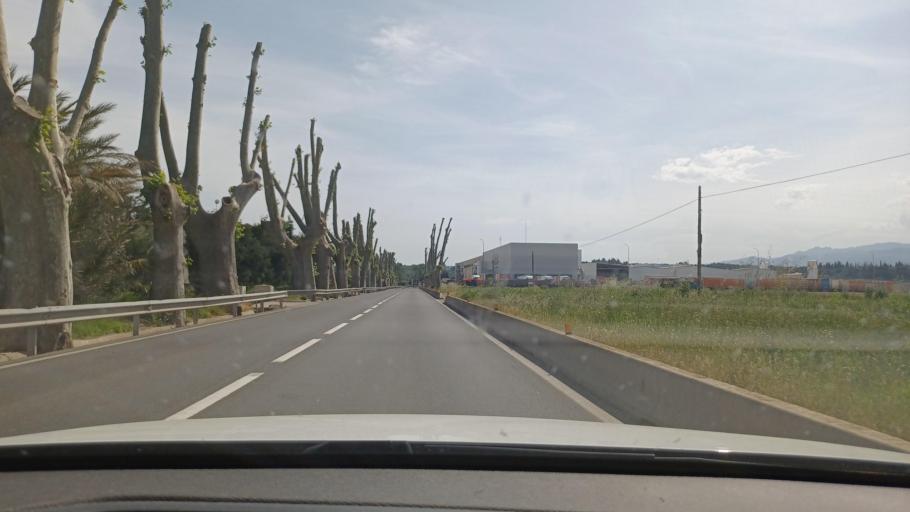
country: ES
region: Catalonia
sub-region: Provincia de Tarragona
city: Tortosa
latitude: 40.7995
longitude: 0.5007
